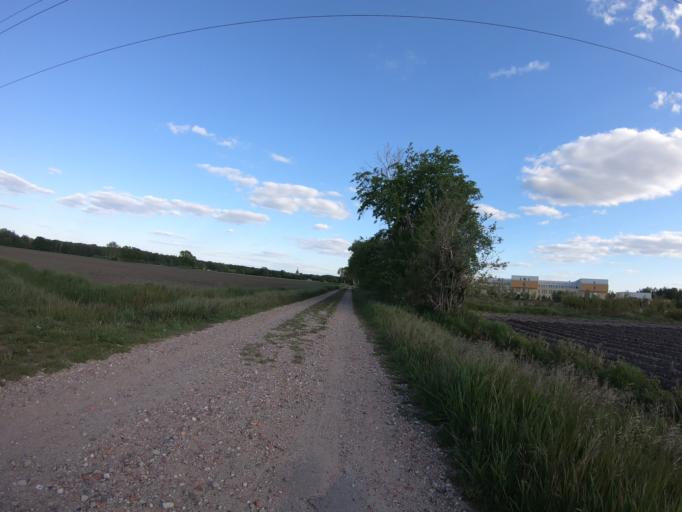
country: DE
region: Lower Saxony
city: Gifhorn
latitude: 52.4997
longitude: 10.5485
